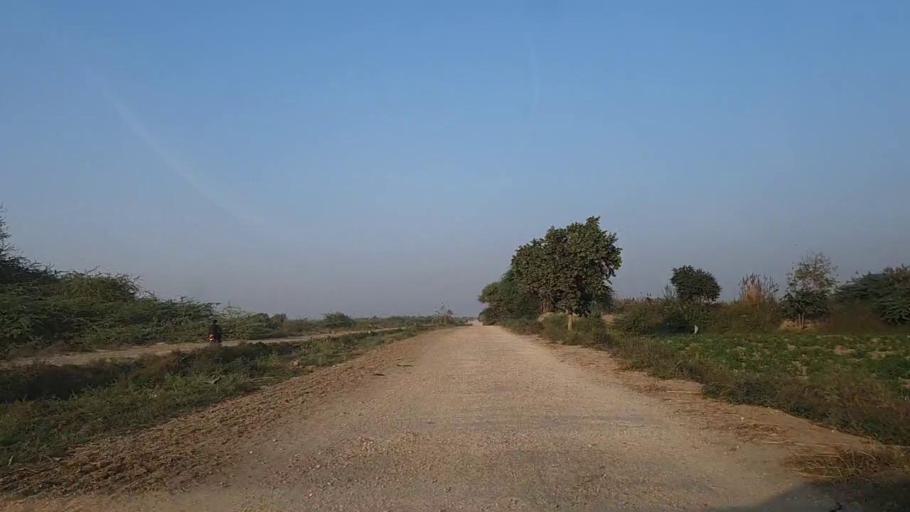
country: PK
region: Sindh
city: Keti Bandar
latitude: 24.2736
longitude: 67.6822
